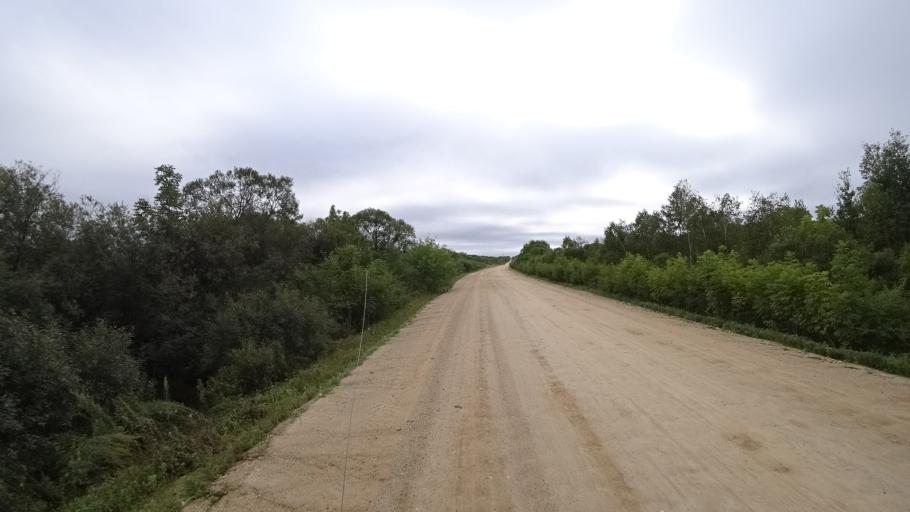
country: RU
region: Primorskiy
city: Rettikhovka
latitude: 44.1226
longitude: 132.6365
